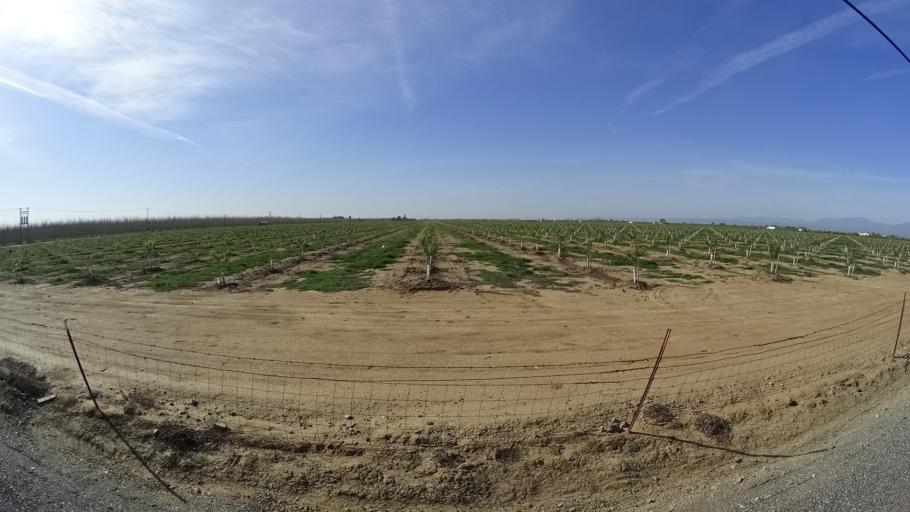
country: US
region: California
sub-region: Glenn County
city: Orland
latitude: 39.6678
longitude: -122.1984
